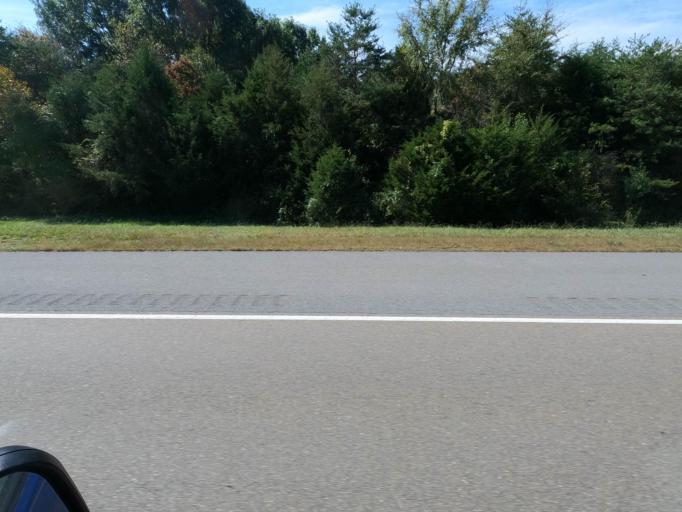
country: US
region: Tennessee
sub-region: Grainger County
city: Bean Station
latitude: 36.3436
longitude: -83.2967
